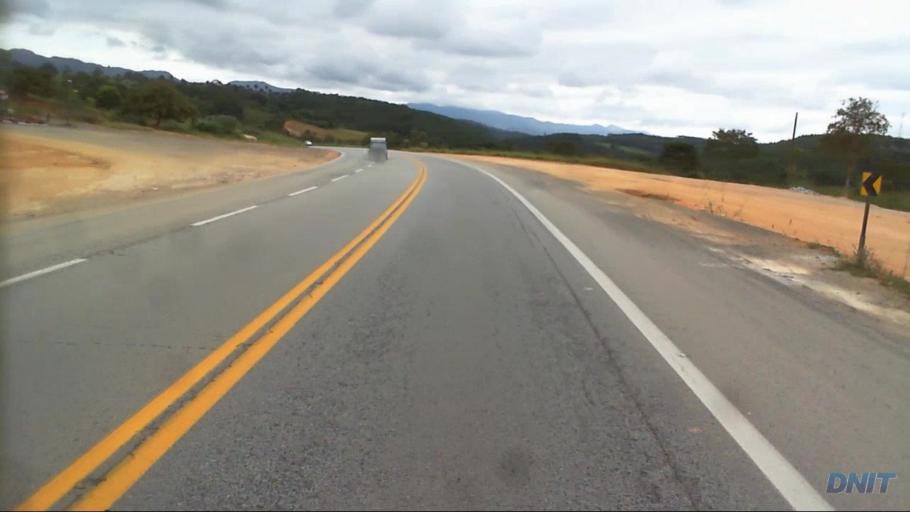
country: BR
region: Minas Gerais
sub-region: Barao De Cocais
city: Barao de Cocais
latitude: -19.7617
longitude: -43.4604
